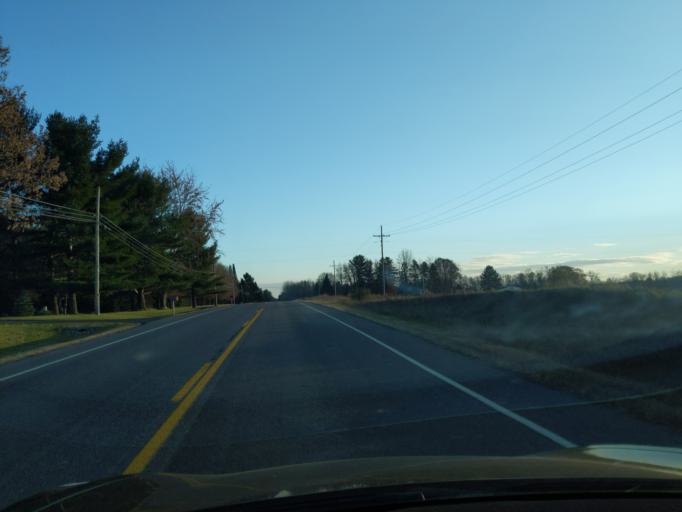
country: US
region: Michigan
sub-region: Ingham County
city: Williamston
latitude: 42.7043
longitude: -84.3145
